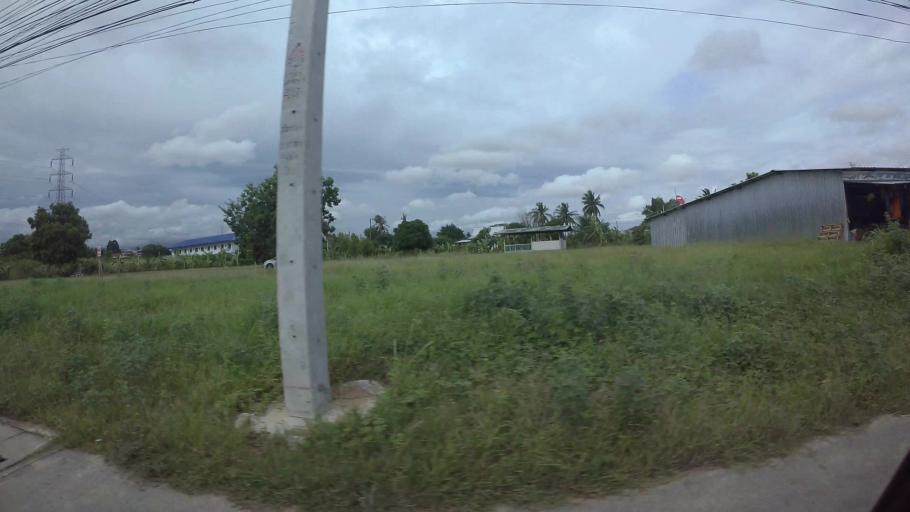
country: TH
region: Chon Buri
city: Si Racha
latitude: 13.1455
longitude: 100.9771
